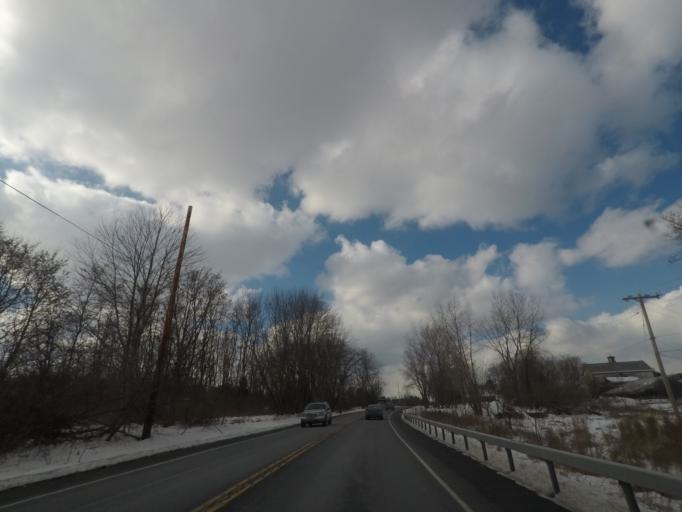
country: US
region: New York
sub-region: Saratoga County
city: Country Knolls
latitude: 42.8681
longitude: -73.8570
